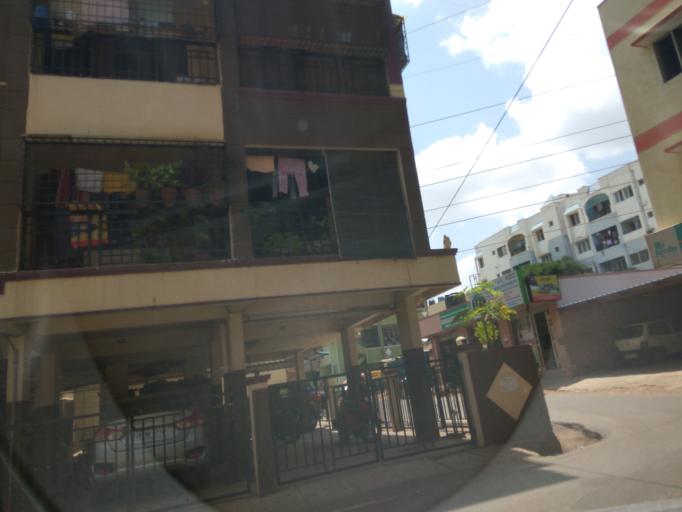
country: IN
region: Karnataka
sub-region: Bangalore Urban
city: Bangalore
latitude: 12.9814
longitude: 77.6754
